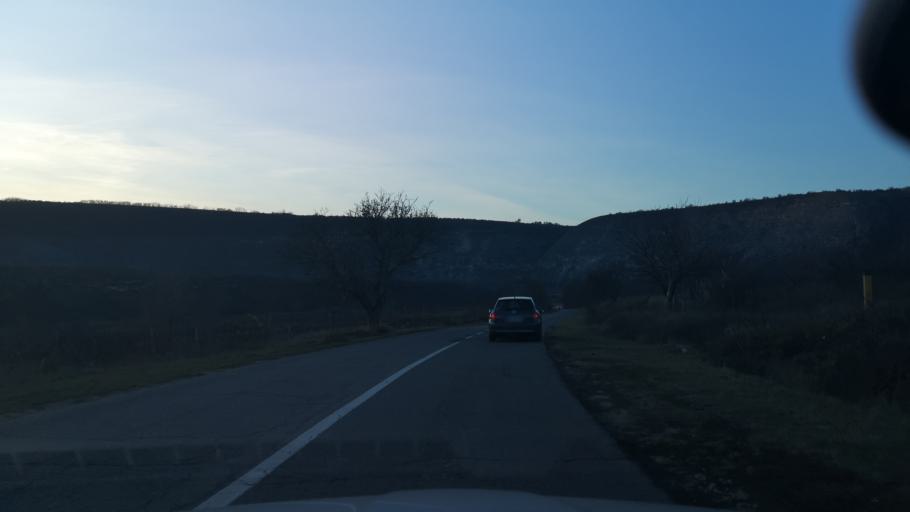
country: MD
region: Telenesti
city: Cocieri
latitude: 47.3057
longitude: 28.9709
